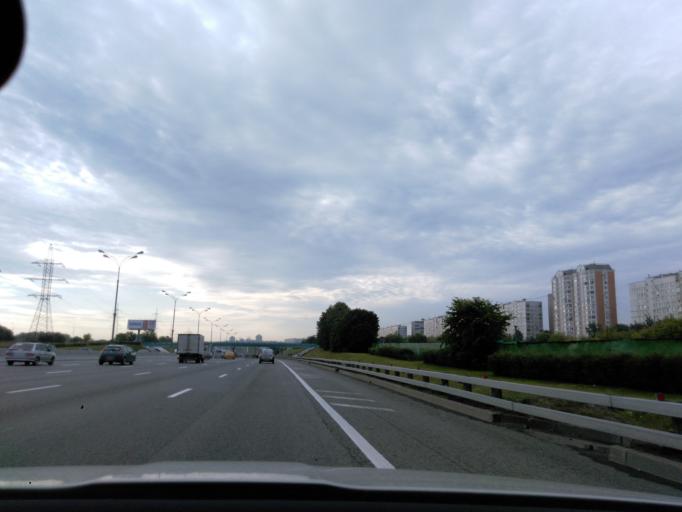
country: RU
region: Moscow
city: Bibirevo
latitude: 55.9037
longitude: 37.6100
